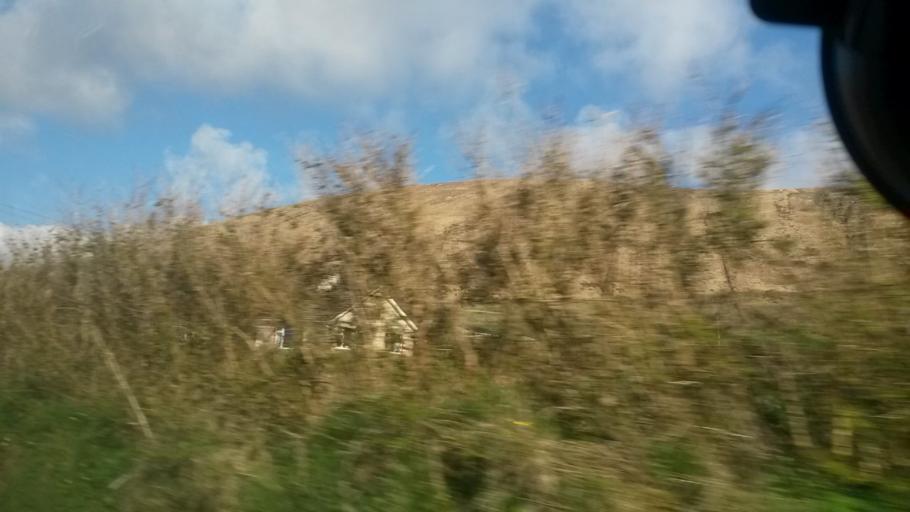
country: IE
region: Munster
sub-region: Ciarrai
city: Dingle
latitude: 52.1523
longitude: -10.4551
